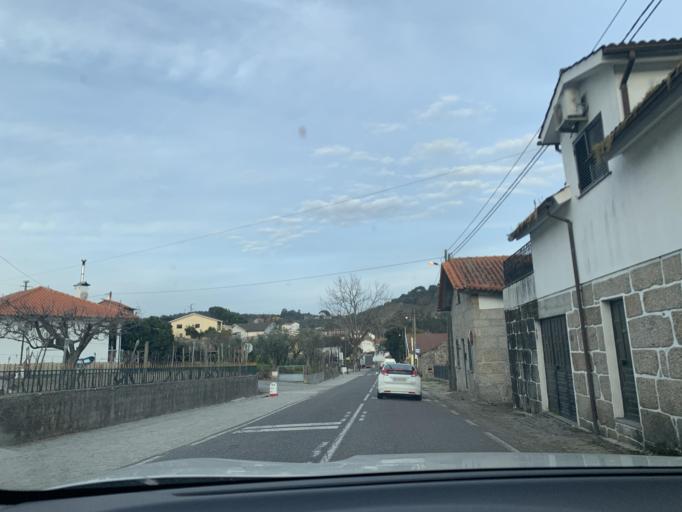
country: PT
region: Viseu
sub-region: Viseu
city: Viseu
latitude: 40.6082
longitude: -7.9762
